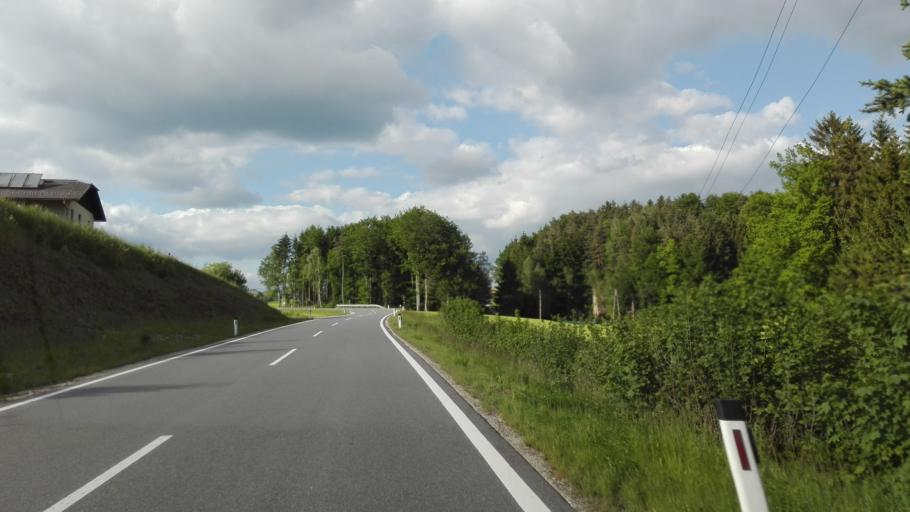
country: AT
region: Upper Austria
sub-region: Politischer Bezirk Perg
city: Perg
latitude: 48.3640
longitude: 14.6817
